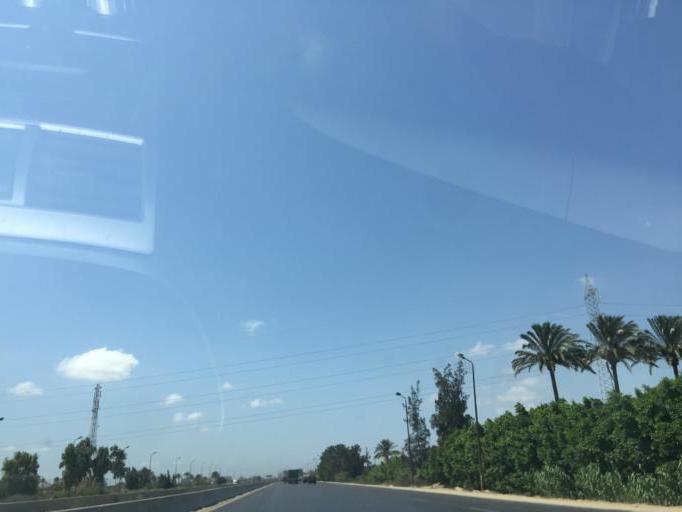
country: EG
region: Alexandria
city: Alexandria
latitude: 30.9914
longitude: 29.8113
